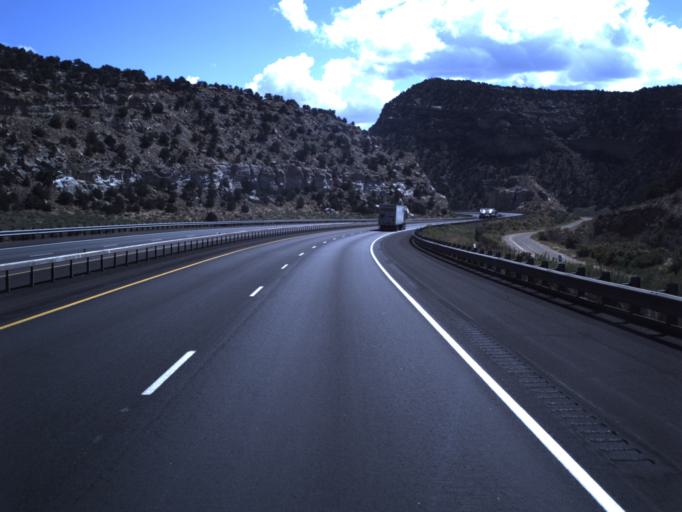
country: US
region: Utah
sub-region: Sevier County
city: Salina
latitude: 38.9127
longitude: -111.7149
